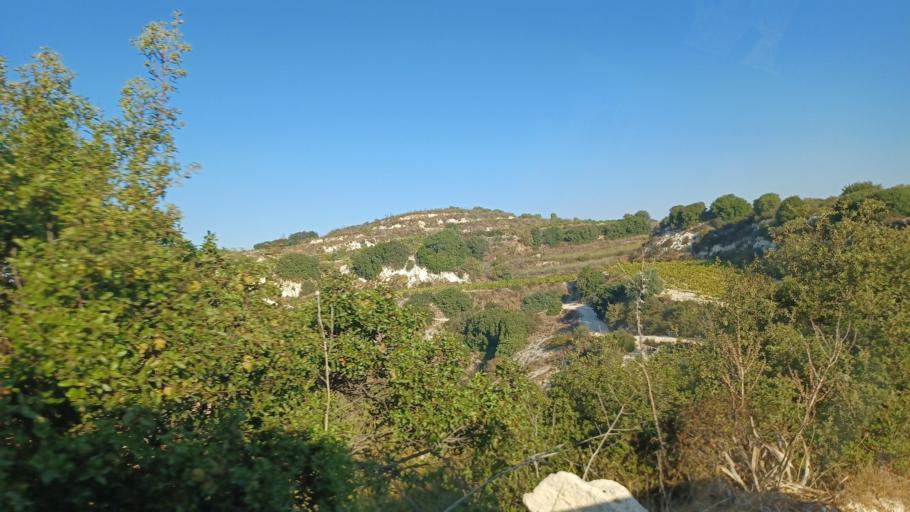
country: CY
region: Pafos
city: Mesogi
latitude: 34.8623
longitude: 32.5130
